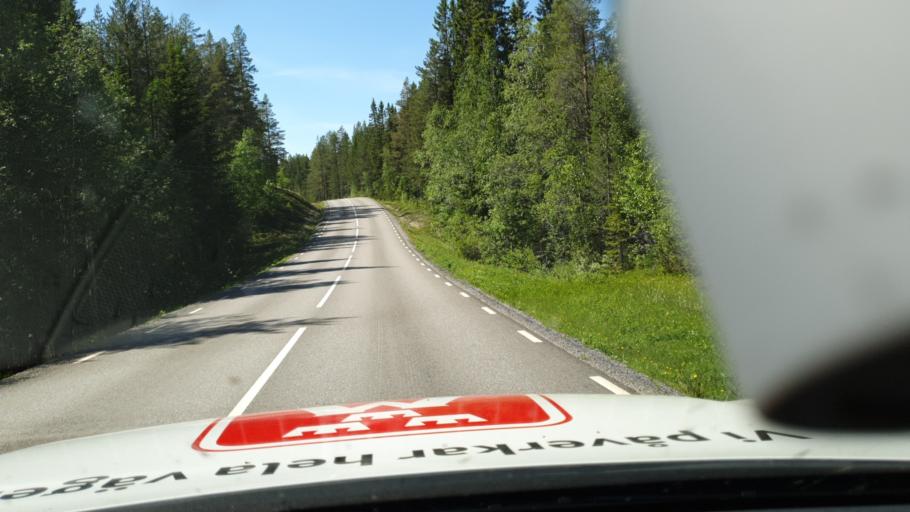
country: SE
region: Jaemtland
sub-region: Harjedalens Kommun
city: Sveg
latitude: 62.1086
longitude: 13.3175
